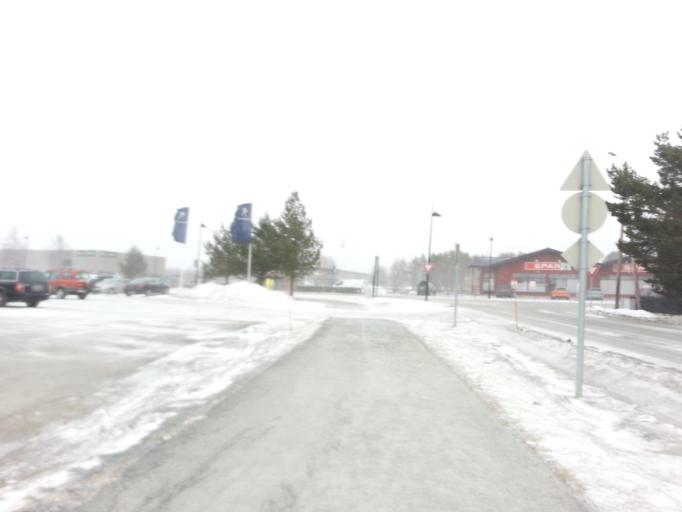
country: NO
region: Sor-Trondelag
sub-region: Oppdal
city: Oppdal
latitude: 62.5915
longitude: 9.6823
